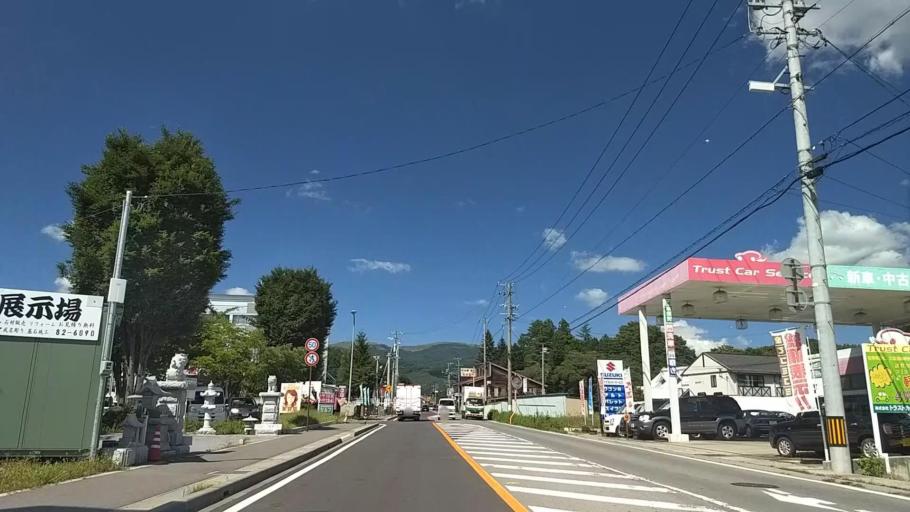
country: JP
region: Nagano
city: Chino
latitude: 36.0120
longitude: 138.1755
